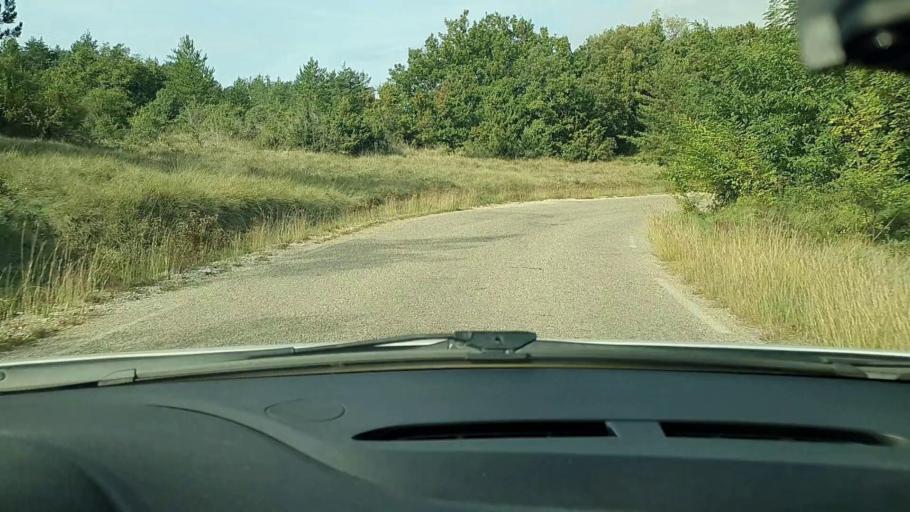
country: FR
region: Languedoc-Roussillon
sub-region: Departement du Gard
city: Saint-Quentin-la-Poterie
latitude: 44.1295
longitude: 4.4015
